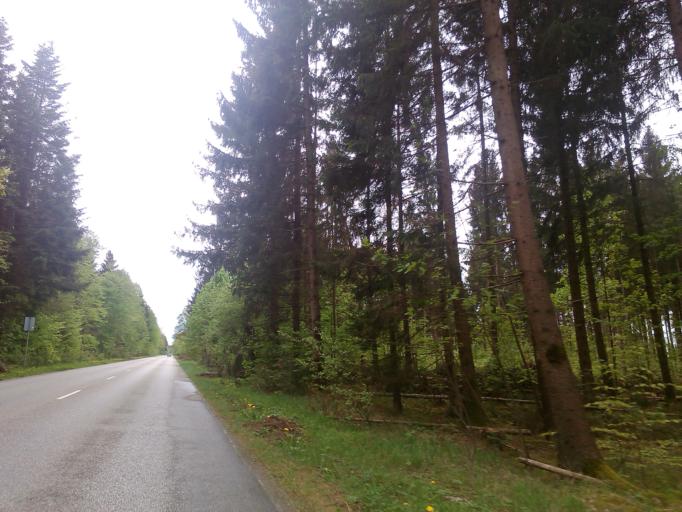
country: DE
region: Bavaria
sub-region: Upper Bavaria
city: Germering
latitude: 48.1117
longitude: 11.3744
